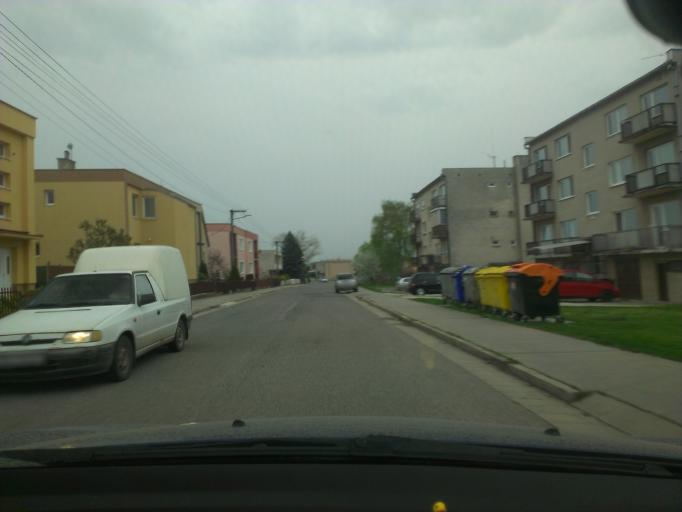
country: SK
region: Trnavsky
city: Vrbove
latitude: 48.6159
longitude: 17.7281
